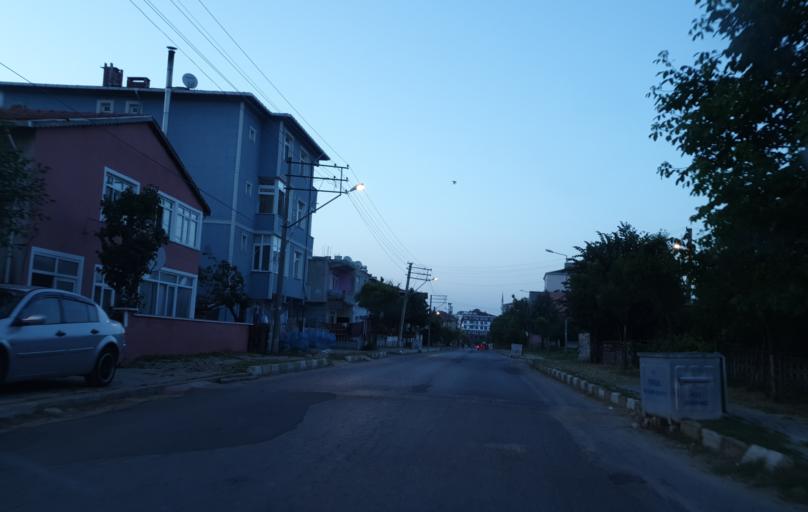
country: TR
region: Tekirdag
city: Saray
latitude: 41.3695
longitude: 27.9295
